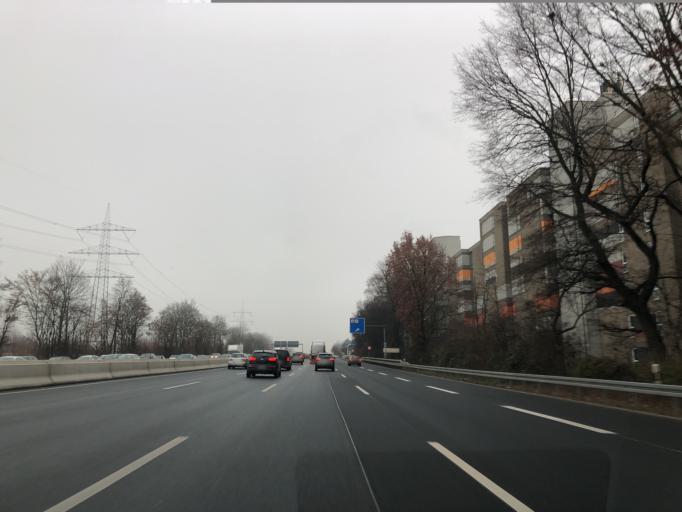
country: DE
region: Hesse
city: Sulzbach
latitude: 50.1166
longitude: 8.5374
